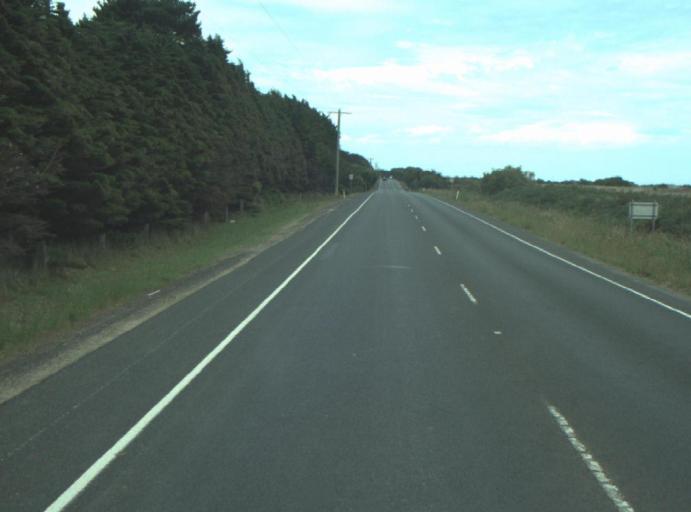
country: AU
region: Victoria
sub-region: Queenscliffe
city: Queenscliff
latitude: -38.2634
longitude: 144.5686
